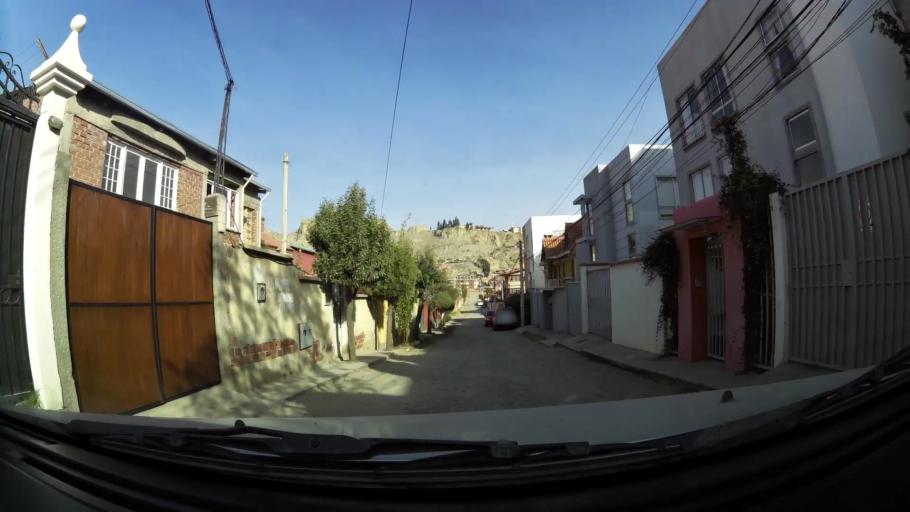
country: BO
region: La Paz
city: La Paz
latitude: -16.5017
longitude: -68.0828
